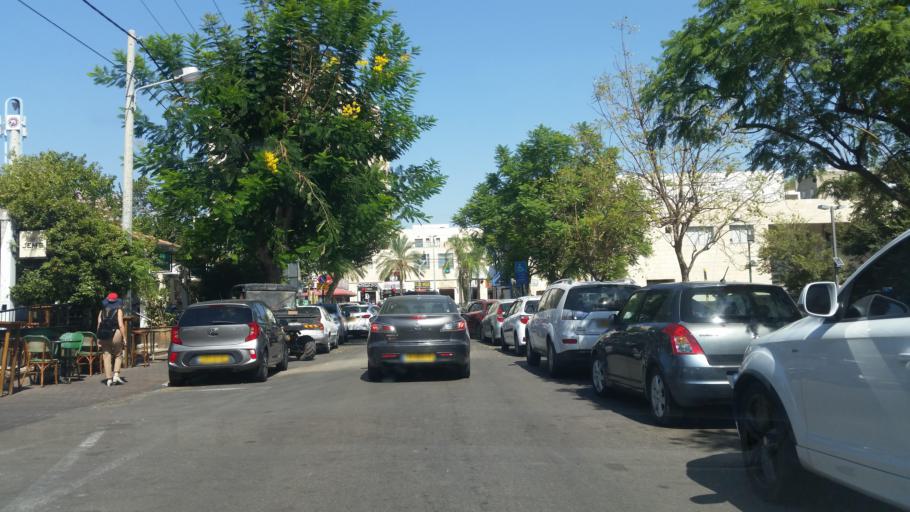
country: IL
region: Central District
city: Ra'anana
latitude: 32.1789
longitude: 34.8781
